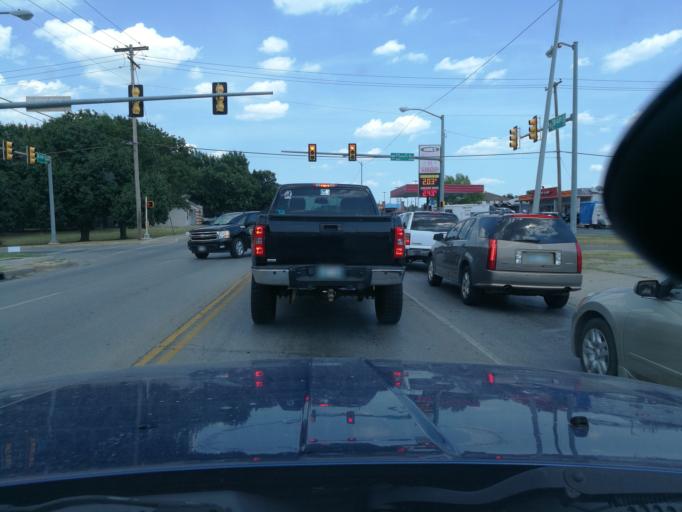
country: US
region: Oklahoma
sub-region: Oklahoma County
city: Oklahoma City
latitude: 35.4207
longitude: -97.5129
